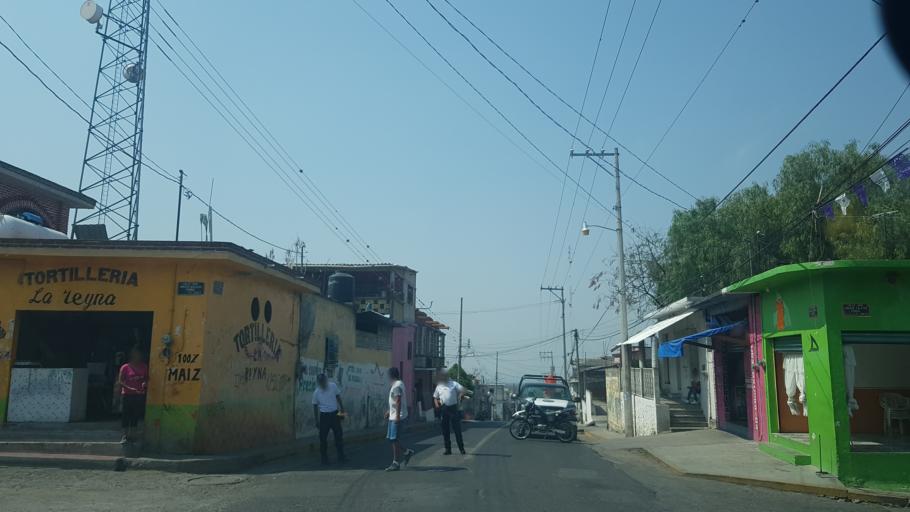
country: MX
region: Morelos
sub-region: Temoac
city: Temoac
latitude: 18.7743
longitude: -98.7771
